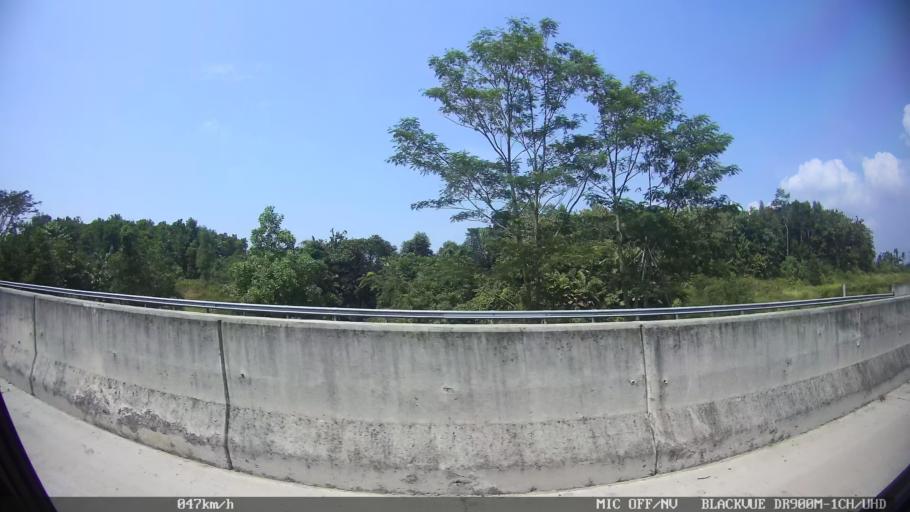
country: ID
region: Lampung
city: Kedaton
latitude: -5.3216
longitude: 105.2724
